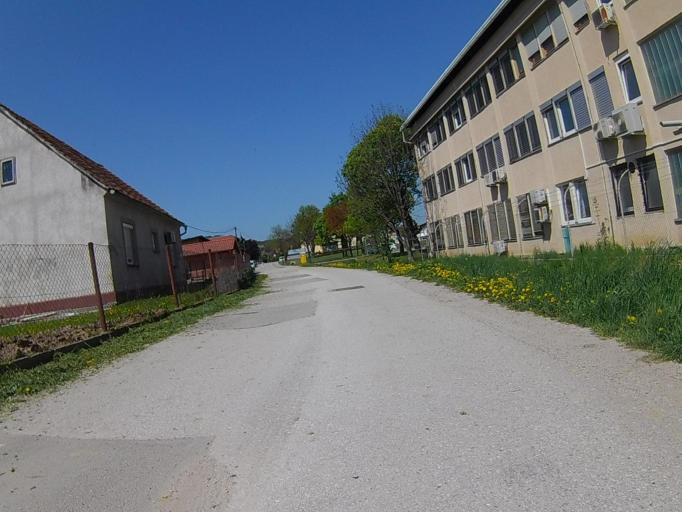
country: SI
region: Hoce-Slivnica
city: Spodnje Hoce
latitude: 46.4976
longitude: 15.6467
